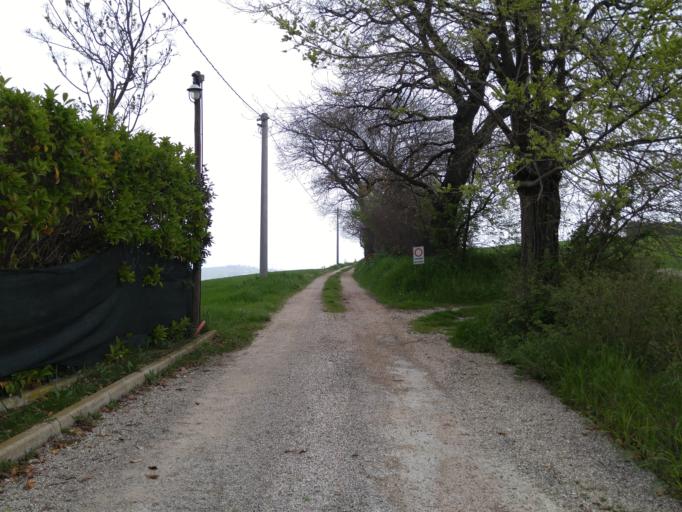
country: IT
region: The Marches
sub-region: Provincia di Pesaro e Urbino
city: Calcinelli
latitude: 43.7698
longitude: 12.9140
